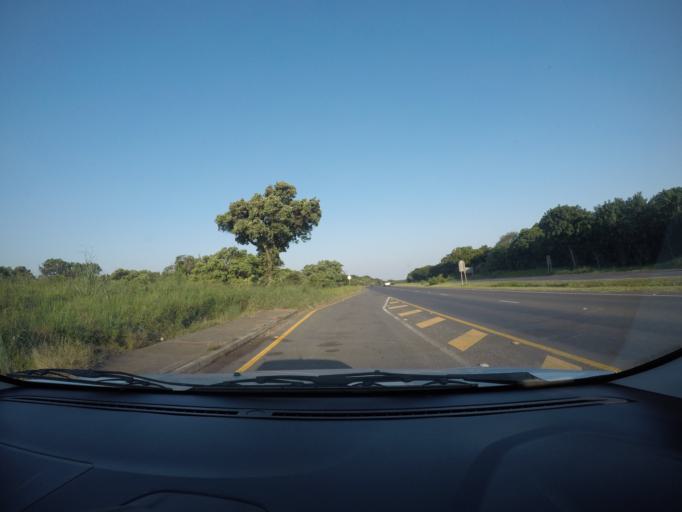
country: ZA
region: KwaZulu-Natal
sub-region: uThungulu District Municipality
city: Richards Bay
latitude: -28.7678
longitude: 32.0497
